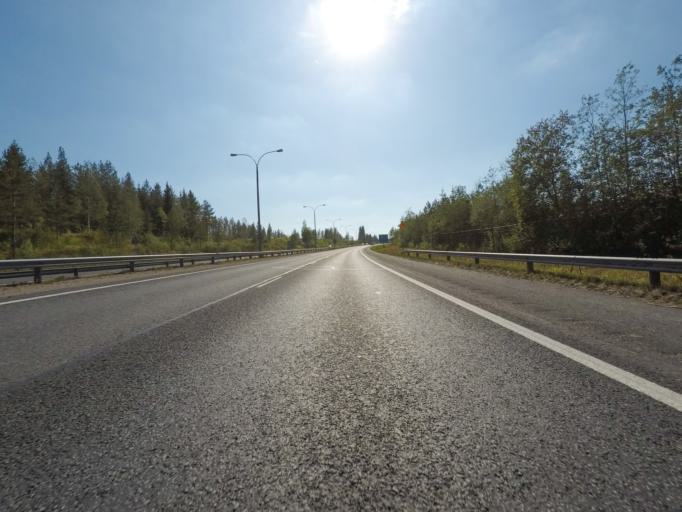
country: FI
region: Northern Savo
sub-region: Kuopio
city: Kuopio
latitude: 62.8137
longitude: 27.6091
